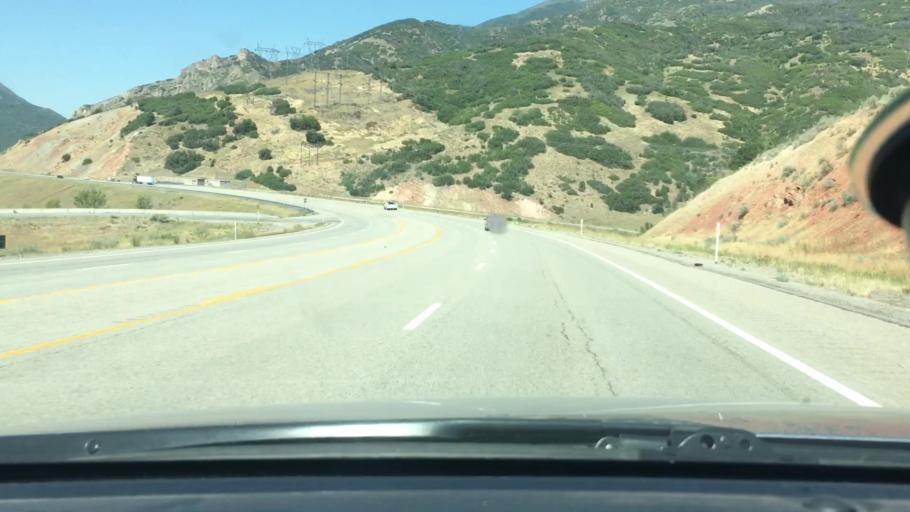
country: US
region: Utah
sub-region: Utah County
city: Mapleton
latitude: 40.0267
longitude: -111.5009
